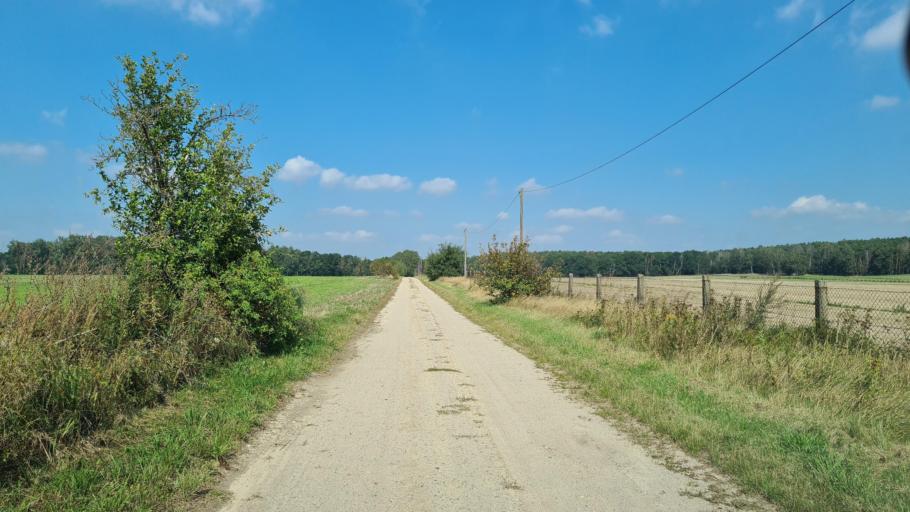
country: DE
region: Brandenburg
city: Sonnewalde
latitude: 51.7222
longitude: 13.6504
